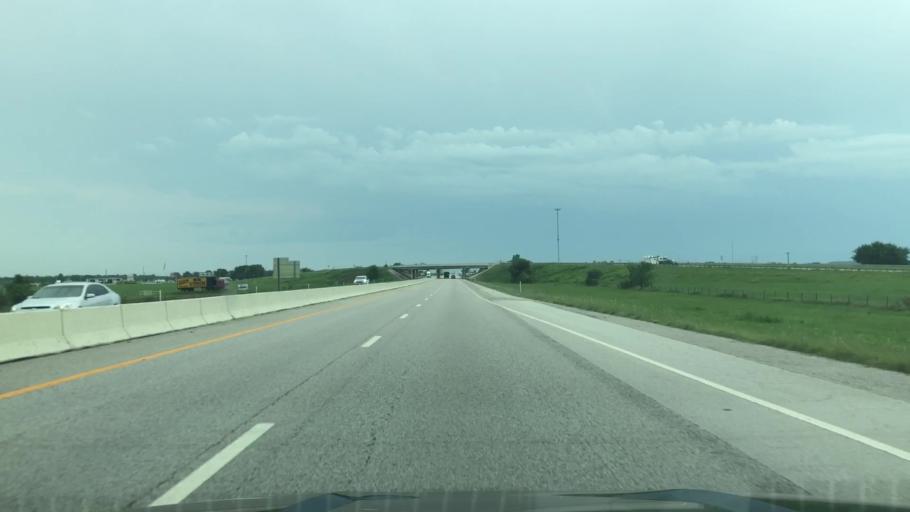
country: US
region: Oklahoma
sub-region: Craig County
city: Vinita
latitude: 36.5614
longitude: -95.2178
